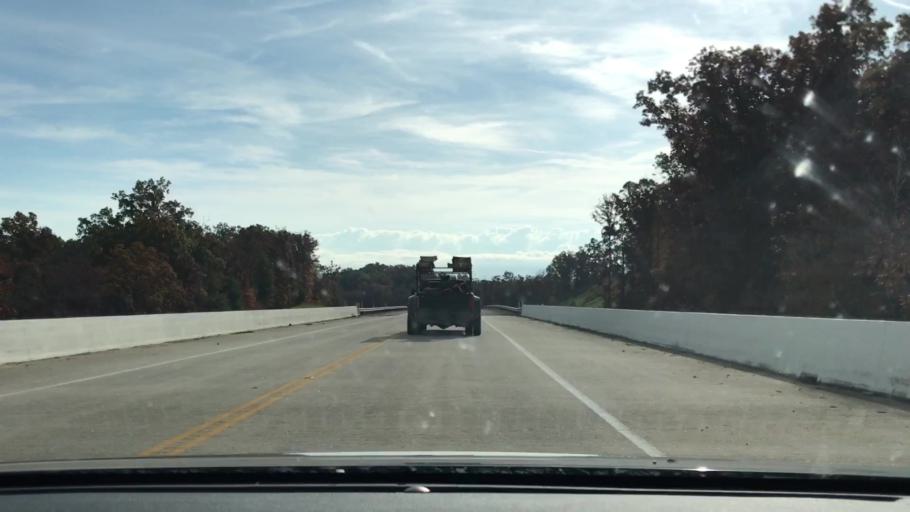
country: US
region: Tennessee
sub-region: Scott County
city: Huntsville
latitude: 36.3489
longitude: -84.7016
